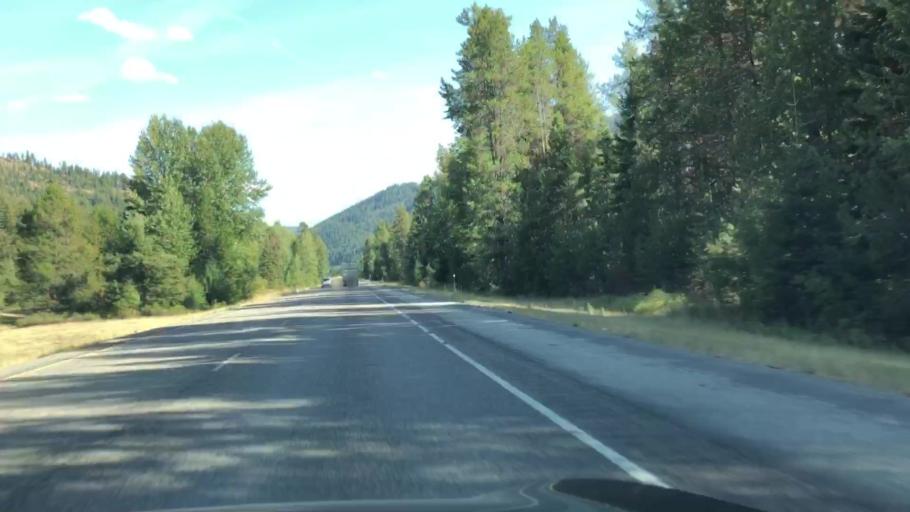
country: US
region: Montana
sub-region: Sanders County
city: Thompson Falls
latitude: 47.3681
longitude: -115.3344
